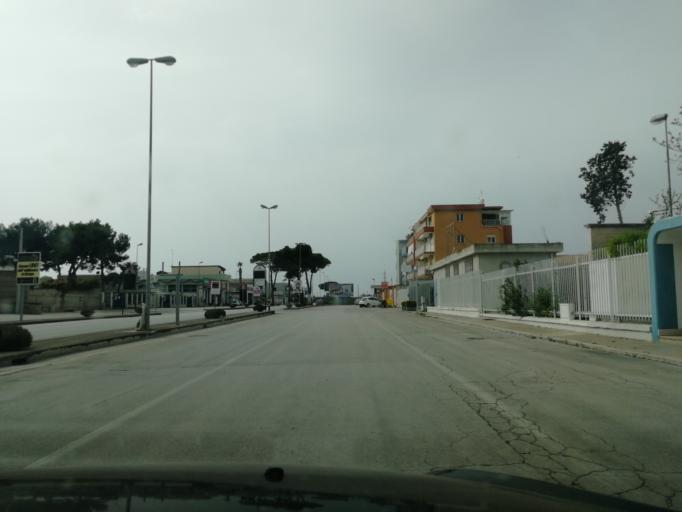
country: IT
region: Apulia
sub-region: Provincia di Barletta - Andria - Trani
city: Barletta
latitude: 41.3110
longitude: 16.3085
